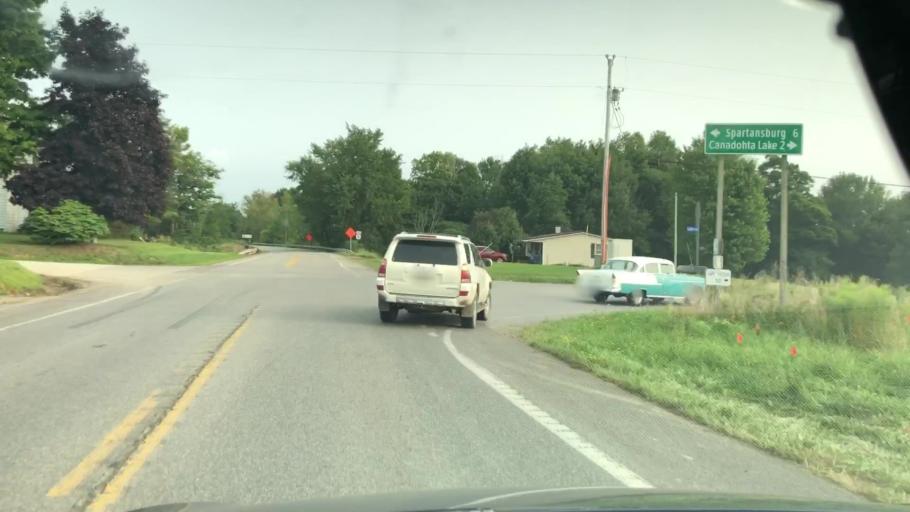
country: US
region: Pennsylvania
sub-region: Erie County
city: Union City
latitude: 41.8201
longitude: -79.8082
